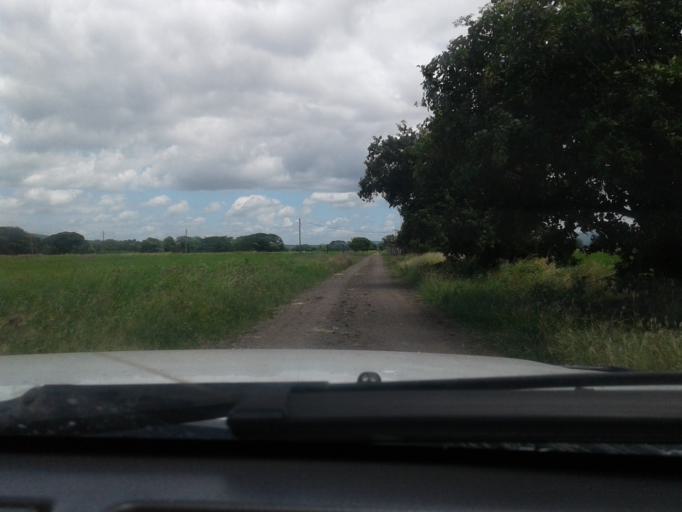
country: NI
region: Matagalpa
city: Ciudad Dario
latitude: 12.8394
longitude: -86.1250
